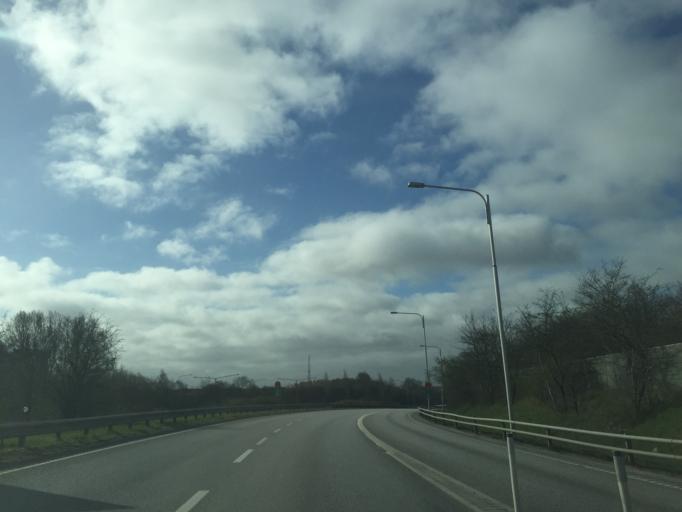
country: SE
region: Skane
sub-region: Malmo
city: Malmoe
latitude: 55.5642
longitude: 13.0003
